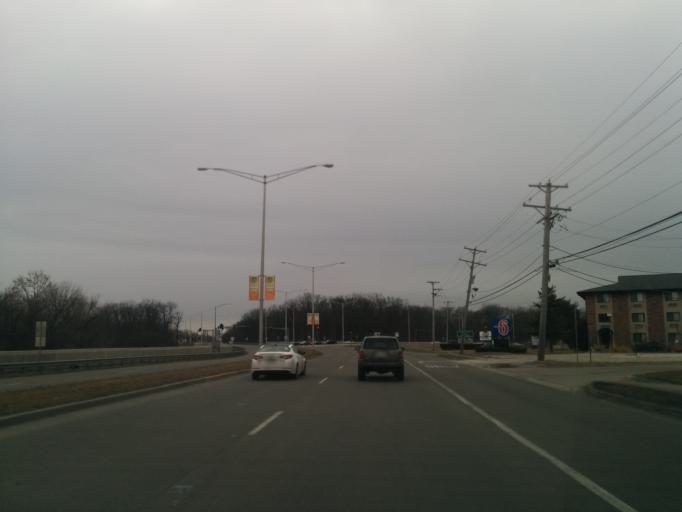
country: US
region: Illinois
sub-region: Cook County
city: Prospect Heights
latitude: 42.1056
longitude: -87.8882
